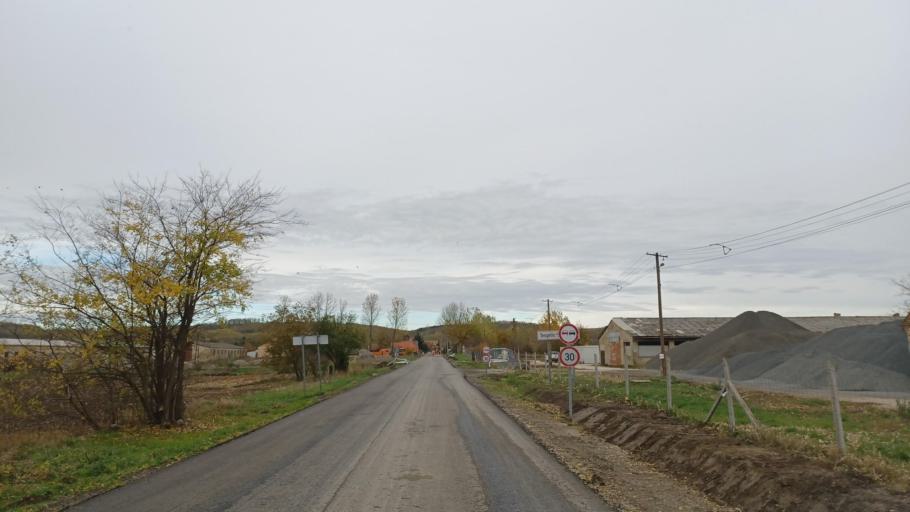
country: HU
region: Tolna
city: Dunaszentgyorgy
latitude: 46.5242
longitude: 18.7716
